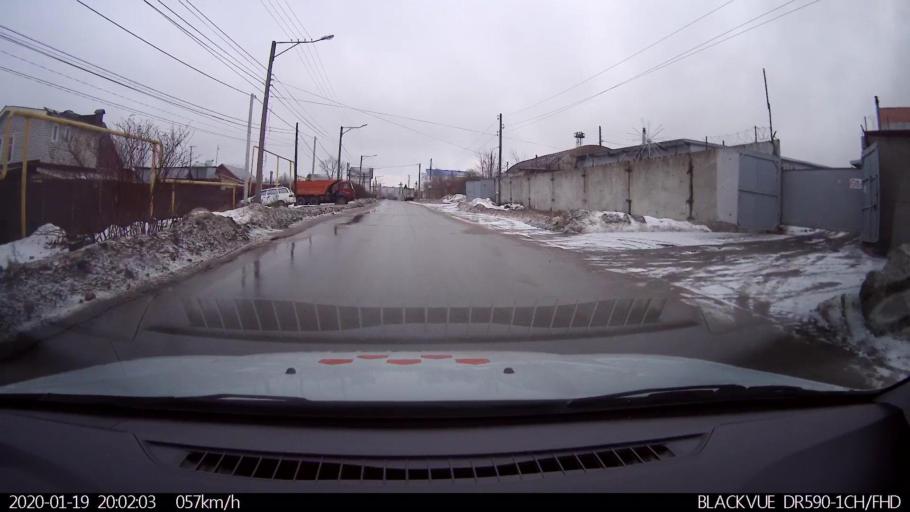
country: RU
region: Nizjnij Novgorod
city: Nizhniy Novgorod
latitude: 56.2347
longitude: 43.9993
